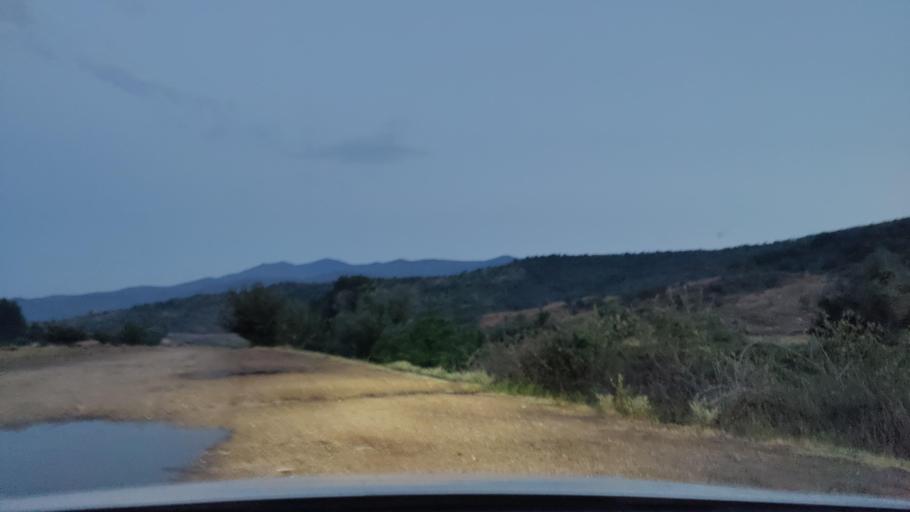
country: GR
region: Central Macedonia
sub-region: Nomos Serron
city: Chrysochorafa
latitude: 41.2058
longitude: 23.0762
